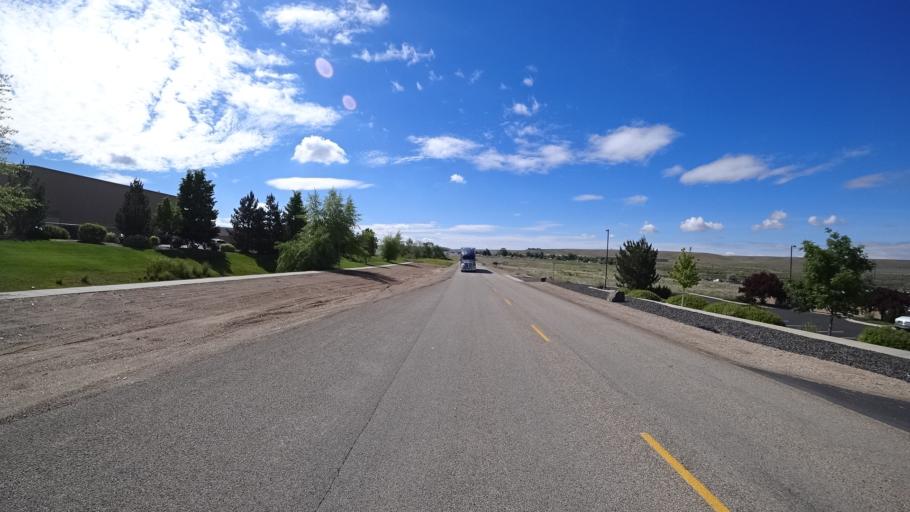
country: US
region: Idaho
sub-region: Ada County
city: Boise
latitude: 43.5341
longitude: -116.1599
